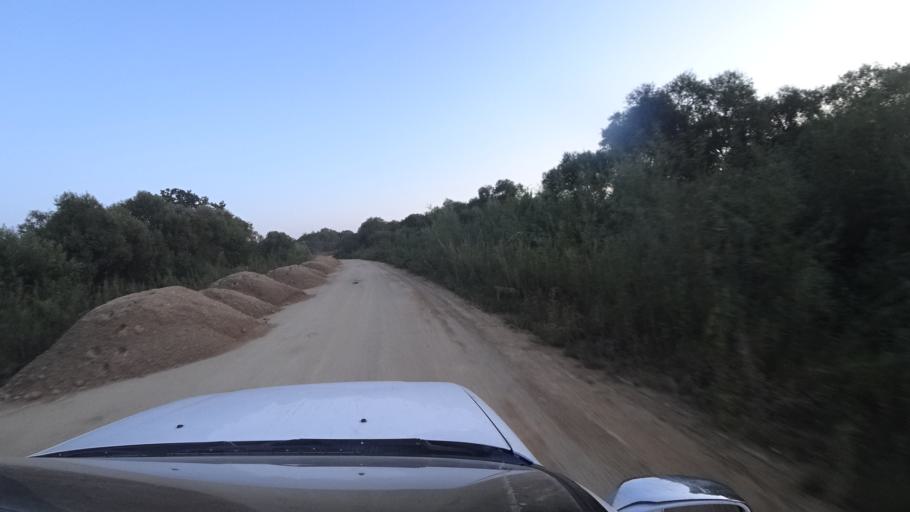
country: RU
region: Primorskiy
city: Dal'nerechensk
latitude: 45.9387
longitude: 133.7602
